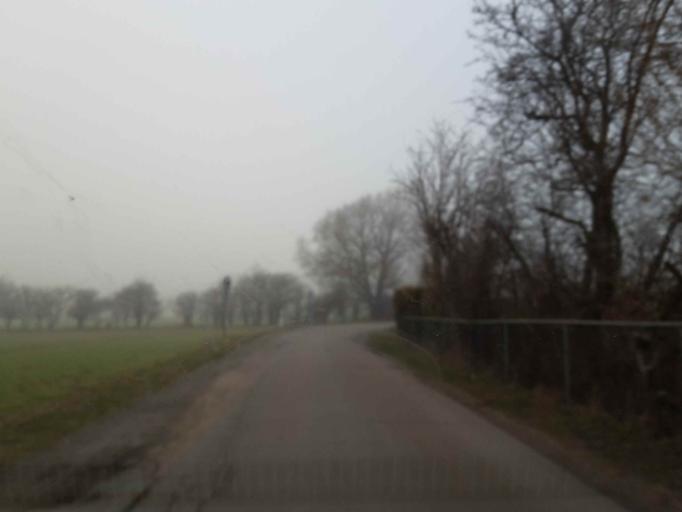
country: DE
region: Schleswig-Holstein
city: Burg auf Fehmarn
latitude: 54.4156
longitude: 11.2428
